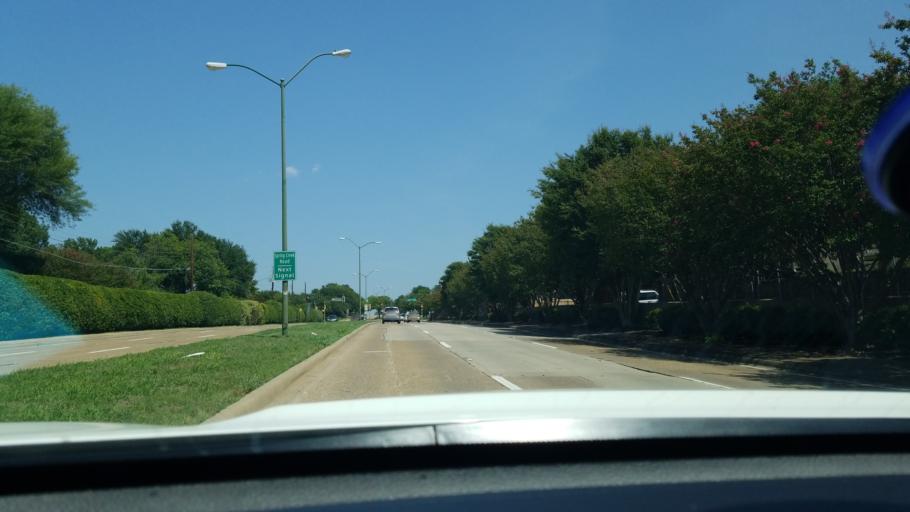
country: US
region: Texas
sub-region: Dallas County
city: Richardson
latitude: 32.9619
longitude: -96.7754
